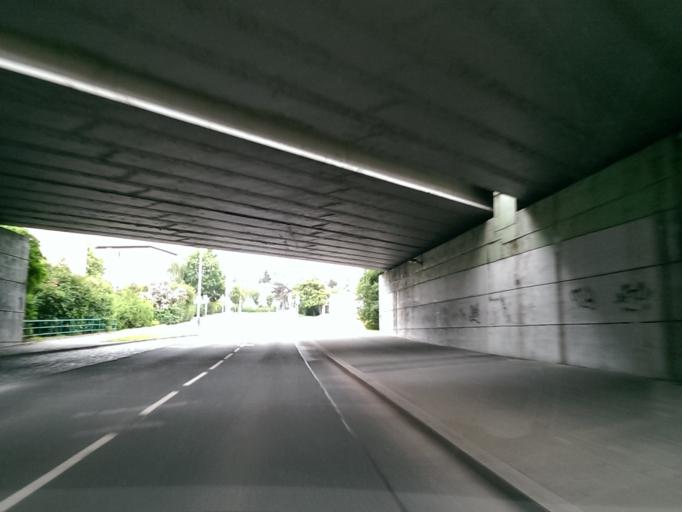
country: CZ
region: Praha
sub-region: Praha 8
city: Karlin
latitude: 50.0454
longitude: 14.4709
